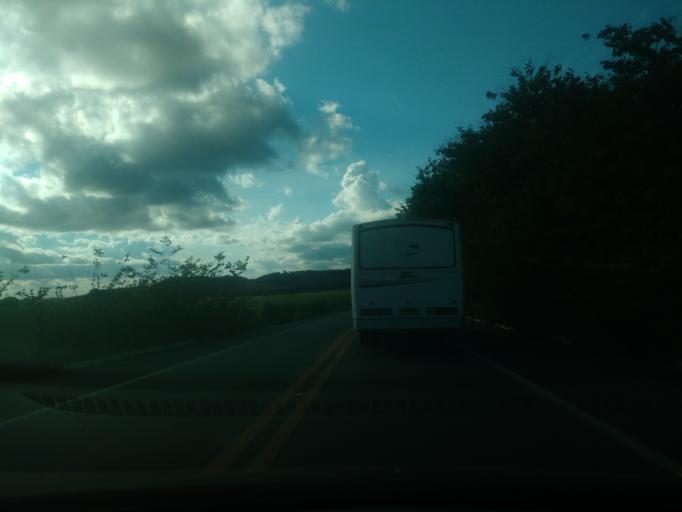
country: BR
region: Alagoas
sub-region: Messias
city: Messias
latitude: -9.3420
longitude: -35.8877
